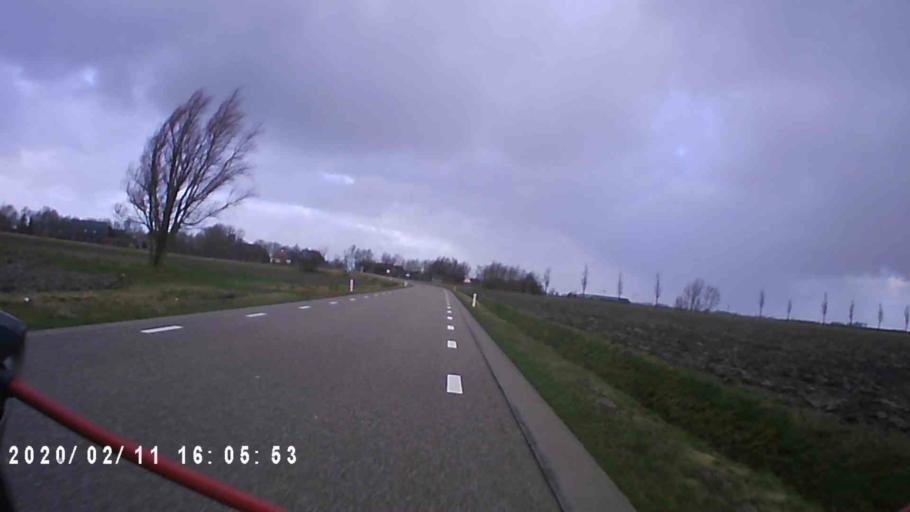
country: NL
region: Groningen
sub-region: Gemeente Zuidhorn
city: Oldehove
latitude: 53.3099
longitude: 6.4223
